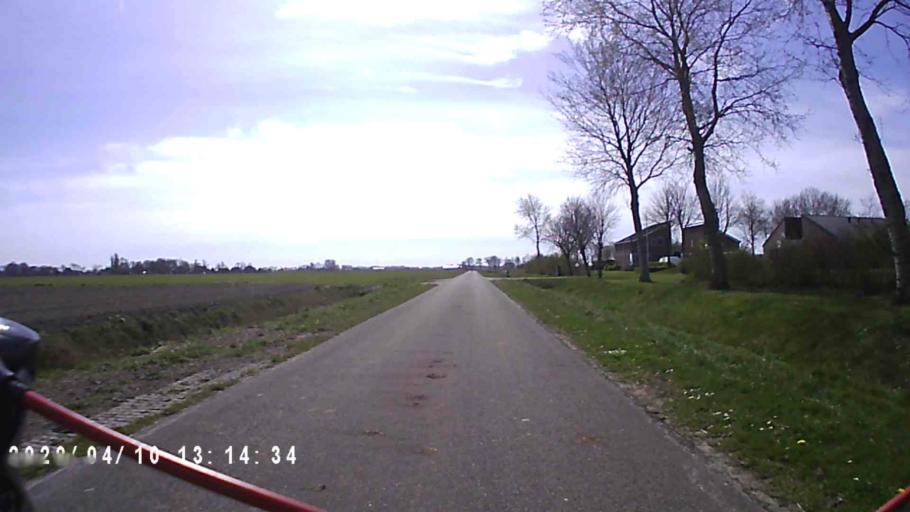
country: NL
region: Groningen
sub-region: Gemeente De Marne
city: Ulrum
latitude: 53.4000
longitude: 6.4173
